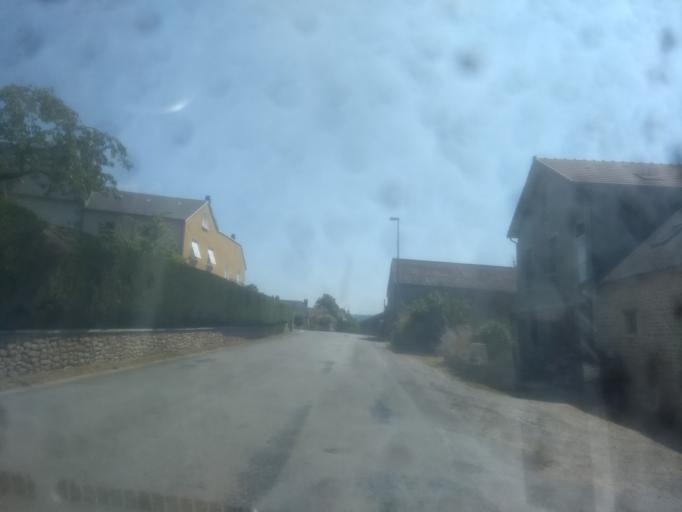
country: FR
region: Limousin
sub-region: Departement de la Haute-Vienne
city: Bessines-sur-Gartempe
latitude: 46.0798
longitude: 1.4255
